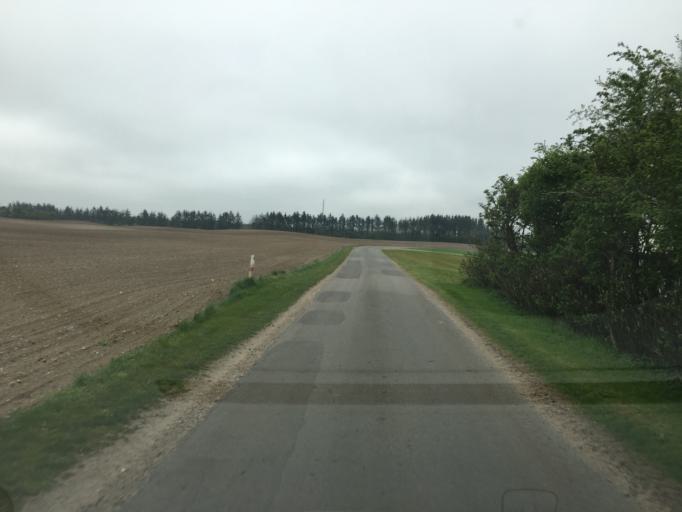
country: DK
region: South Denmark
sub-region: Aabenraa Kommune
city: Krusa
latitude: 54.8843
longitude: 9.4021
